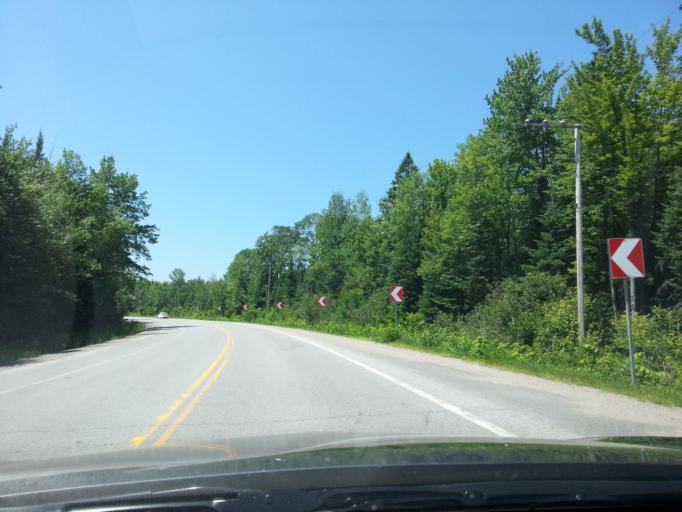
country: CA
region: Ontario
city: Arnprior
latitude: 45.5498
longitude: -76.3583
